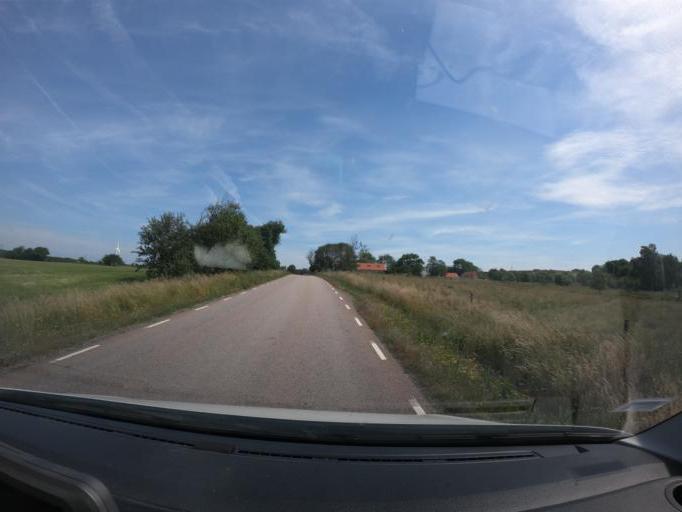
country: SE
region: Skane
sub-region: Bastads Kommun
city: Forslov
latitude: 56.4182
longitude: 12.7620
